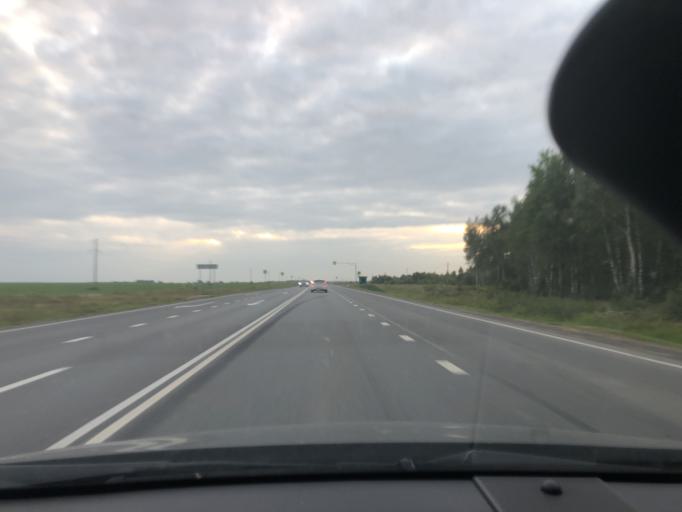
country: RU
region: Tula
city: Khanino
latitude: 54.3816
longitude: 36.6361
